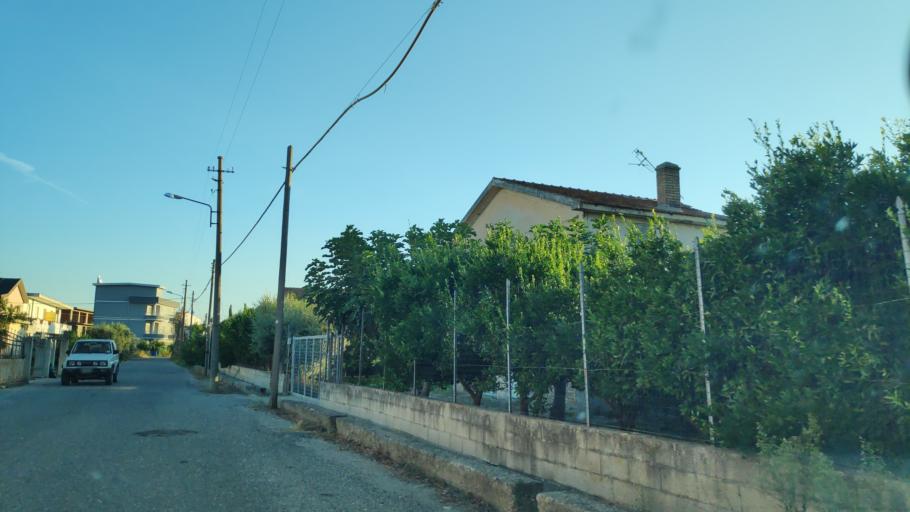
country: IT
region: Calabria
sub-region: Provincia di Reggio Calabria
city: Monasterace Marina
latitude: 38.4329
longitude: 16.5639
